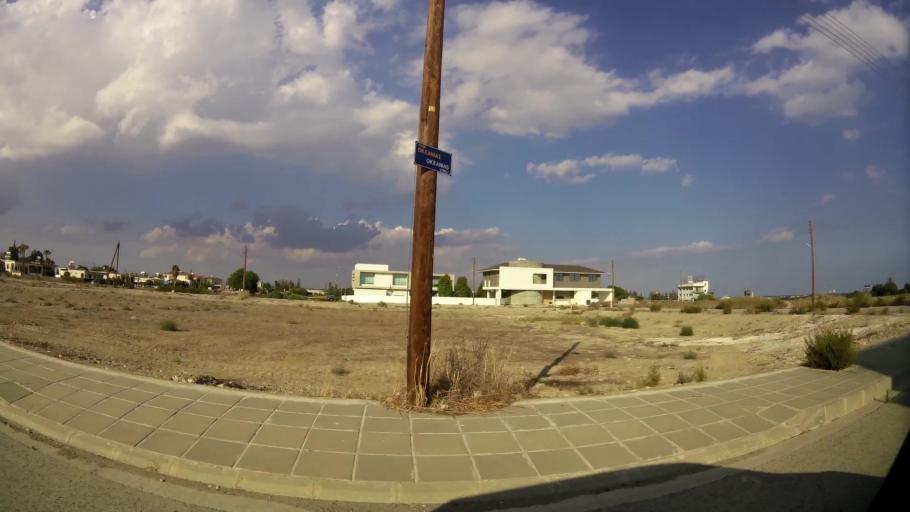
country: CY
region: Larnaka
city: Dhromolaxia
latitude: 34.8801
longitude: 33.5905
